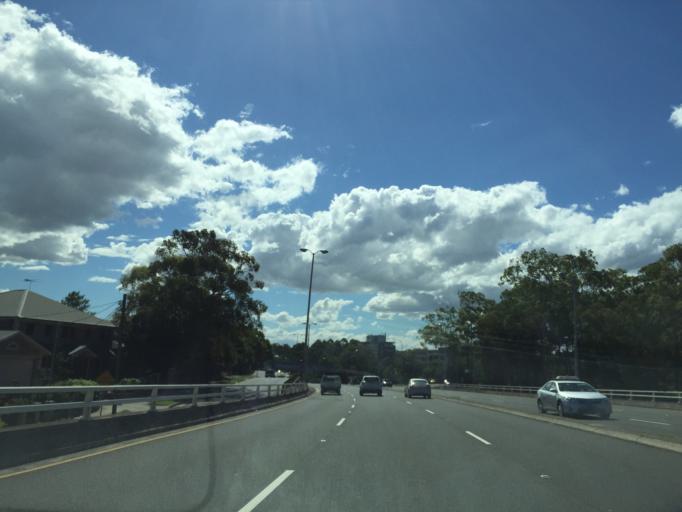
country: AU
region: New South Wales
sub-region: Ryde
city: North Ryde
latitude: -33.7868
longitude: 151.1245
